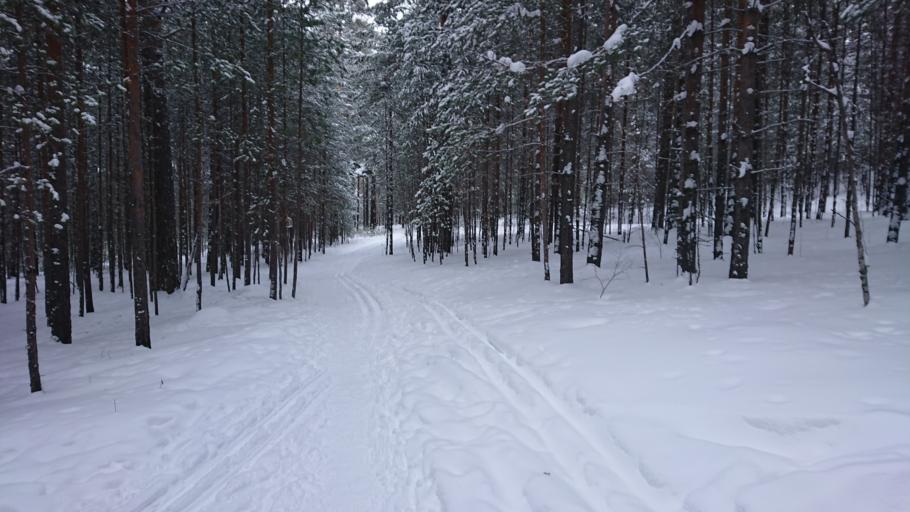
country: RU
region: Sverdlovsk
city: Degtyarsk
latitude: 56.6954
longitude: 60.0657
